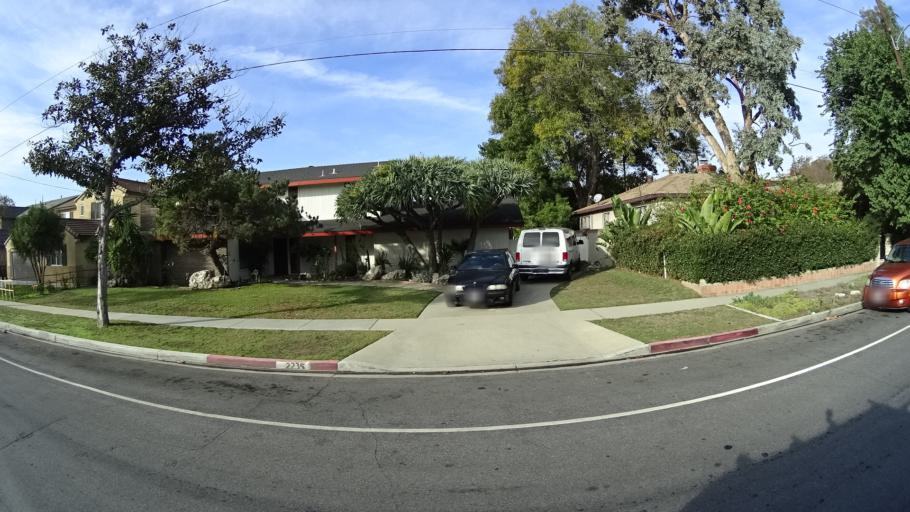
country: US
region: California
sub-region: Orange County
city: Garden Grove
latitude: 33.7929
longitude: -117.9369
